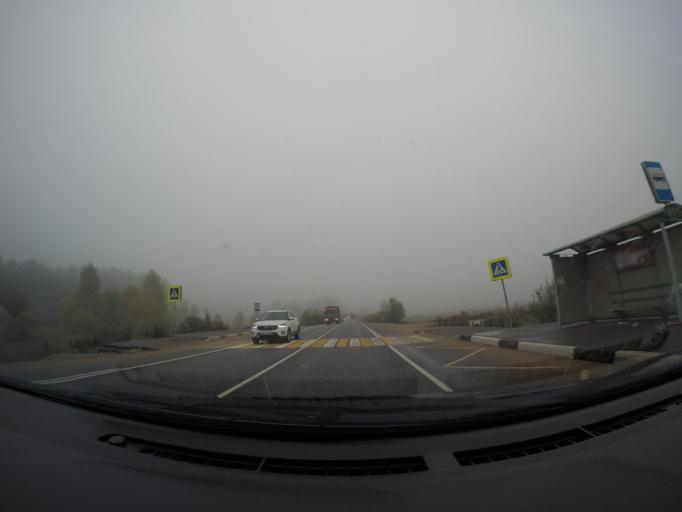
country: RU
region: Moskovskaya
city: Novopetrovskoye
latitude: 55.8341
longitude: 36.4488
